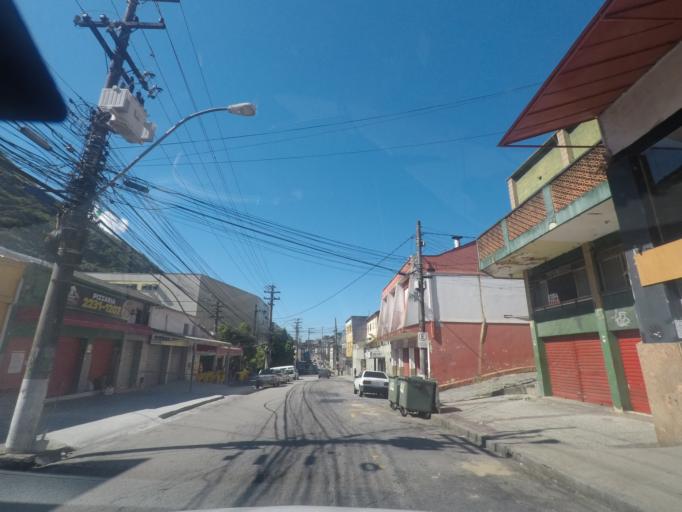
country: BR
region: Rio de Janeiro
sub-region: Petropolis
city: Petropolis
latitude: -22.5227
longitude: -43.1706
